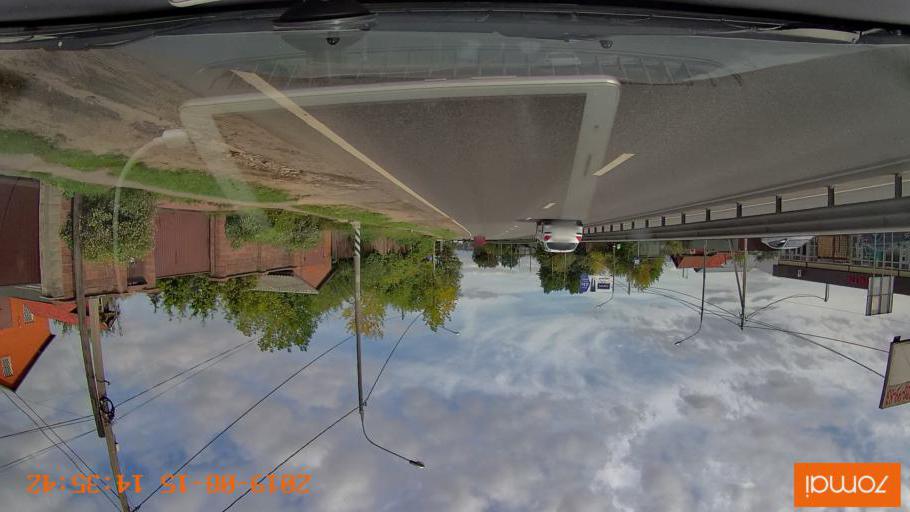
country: RU
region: Moskovskaya
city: Tomilino
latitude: 55.6404
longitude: 37.9372
